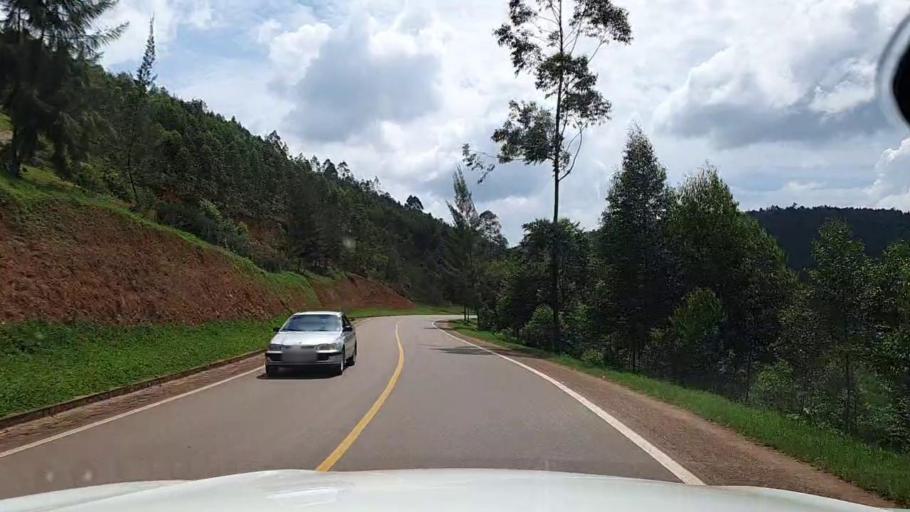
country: RW
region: Kigali
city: Kigali
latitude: -1.8166
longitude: 30.1096
